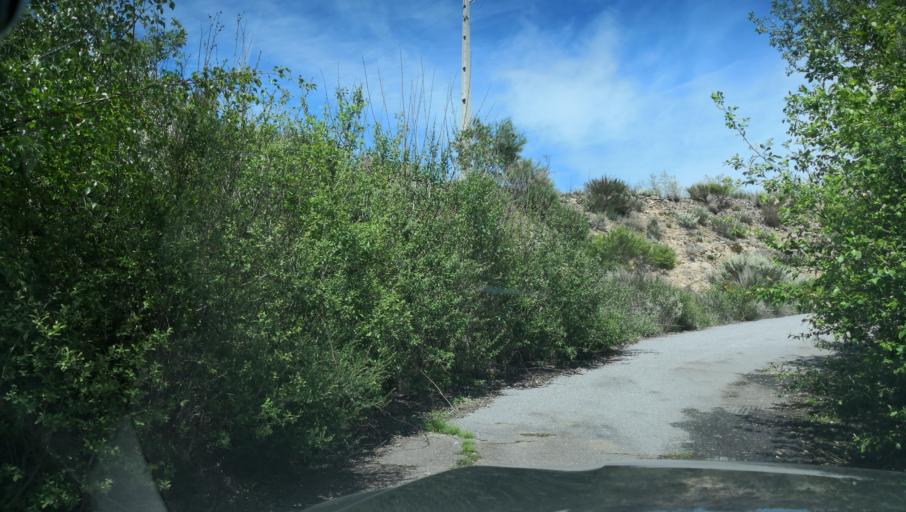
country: PT
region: Vila Real
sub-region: Vila Real
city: Vila Real
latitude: 41.3721
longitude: -7.6781
